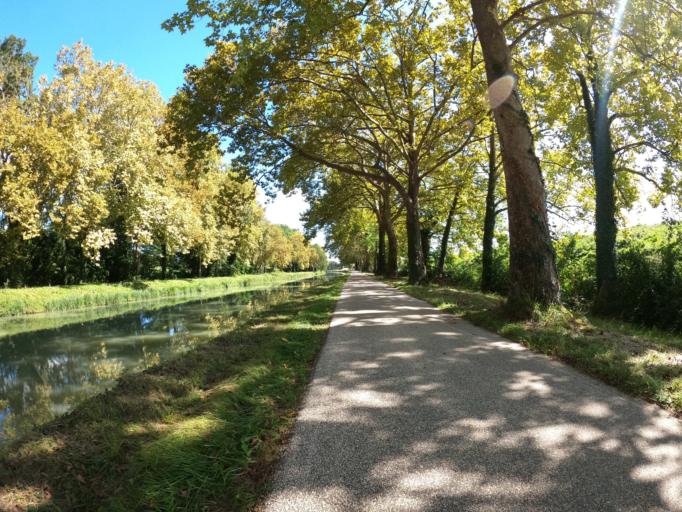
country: FR
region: Midi-Pyrenees
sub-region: Departement du Tarn-et-Garonne
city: Valence
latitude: 44.1011
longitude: 0.9113
